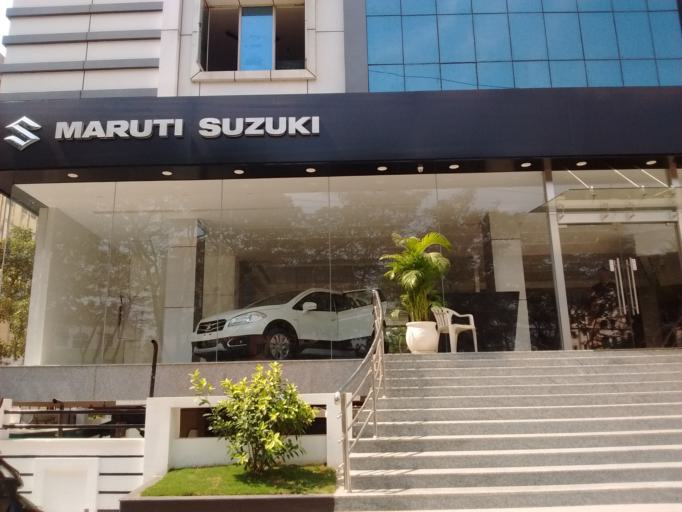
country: IN
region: Andhra Pradesh
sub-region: Krishna
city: Yanamalakuduru
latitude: 16.5122
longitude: 80.6671
